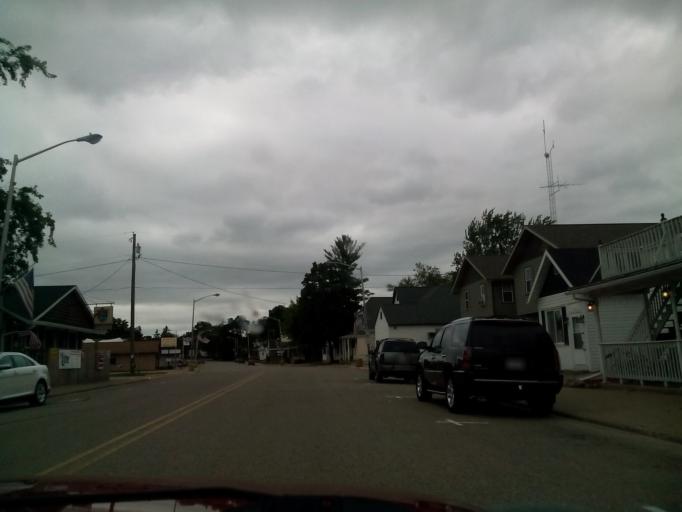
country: US
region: Wisconsin
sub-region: Waupaca County
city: Weyauwega
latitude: 44.2605
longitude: -88.8654
